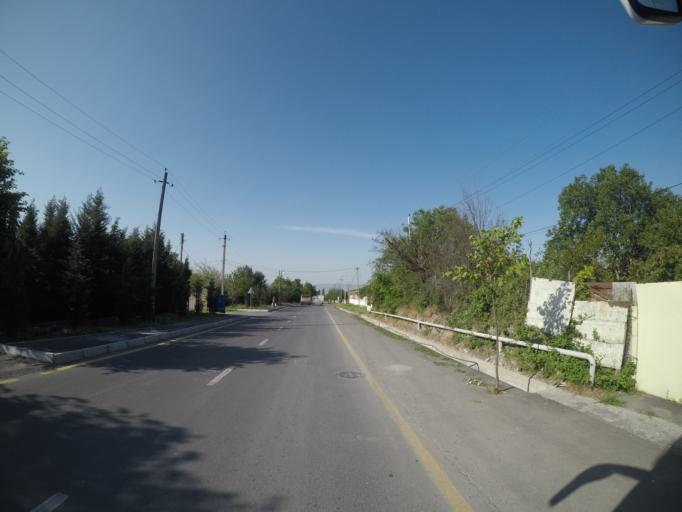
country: AZ
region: Shaki City
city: Sheki
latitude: 41.2157
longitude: 47.1683
